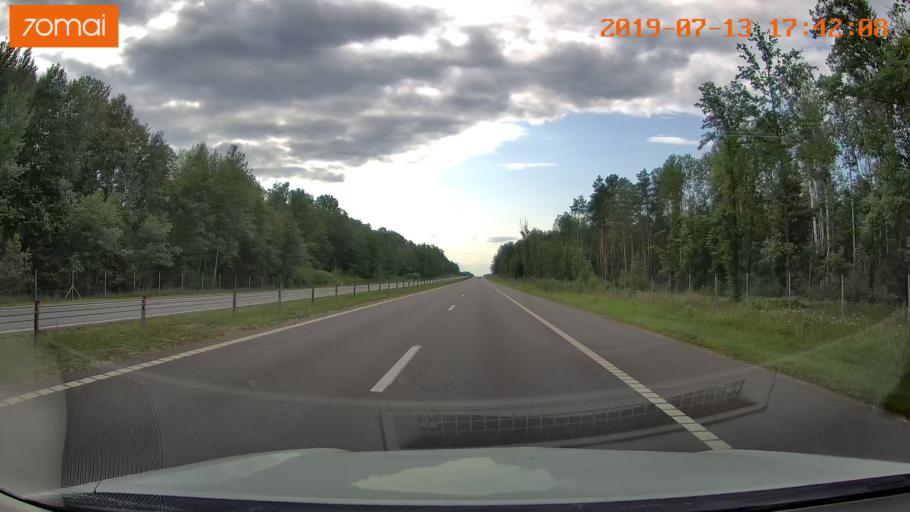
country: BY
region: Mogilev
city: Asipovichy
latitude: 53.2998
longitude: 28.7850
